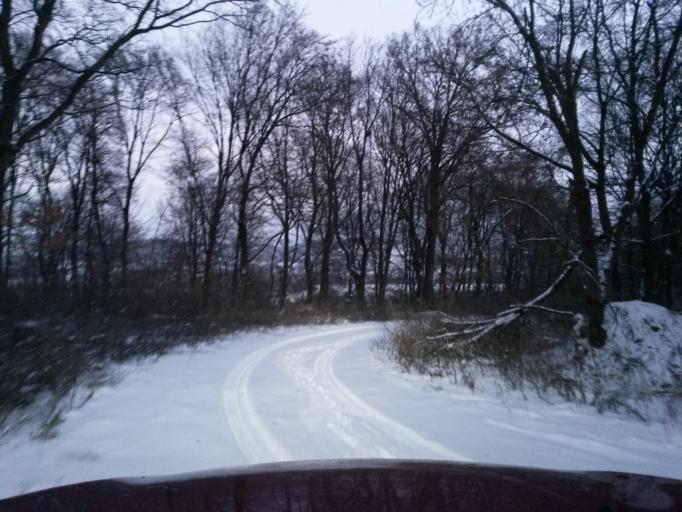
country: SK
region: Kosicky
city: Kosice
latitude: 48.7347
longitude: 21.3241
